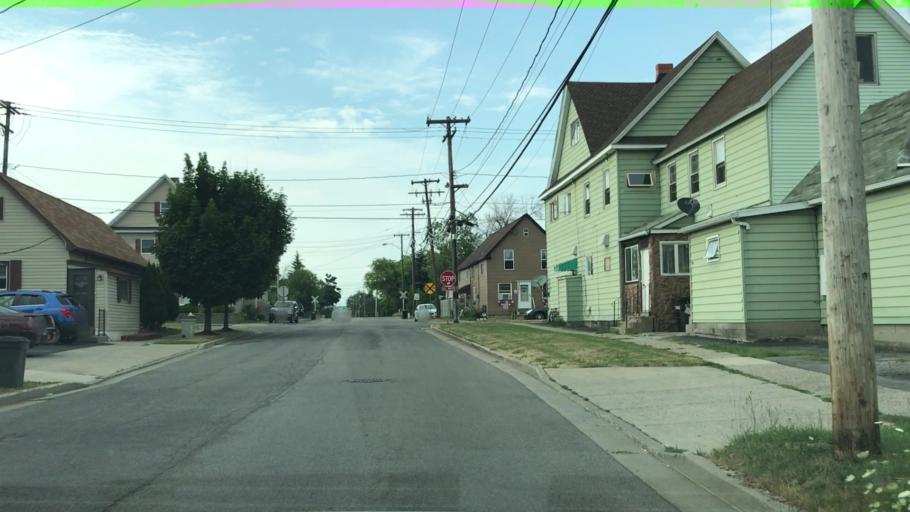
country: US
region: New York
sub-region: Erie County
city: Lancaster
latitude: 42.9089
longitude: -78.6783
